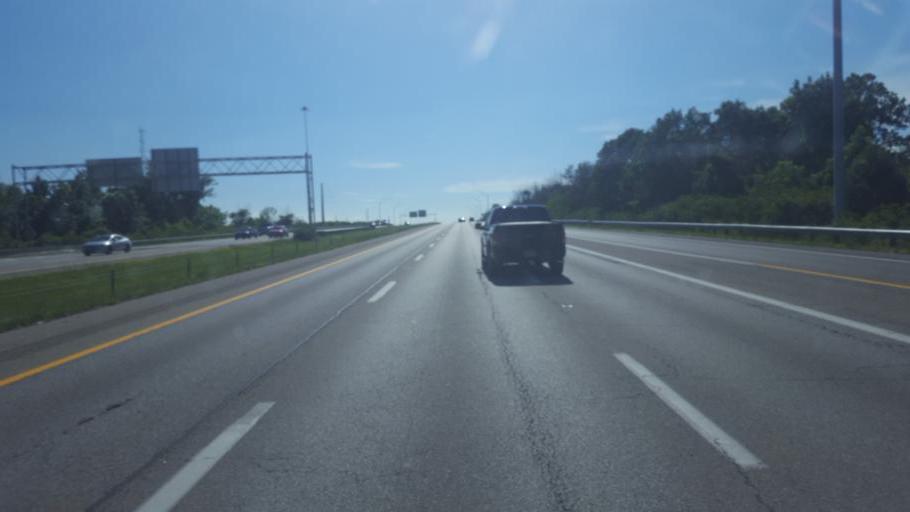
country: US
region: Ohio
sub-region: Franklin County
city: Whitehall
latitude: 39.9365
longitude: -82.8824
